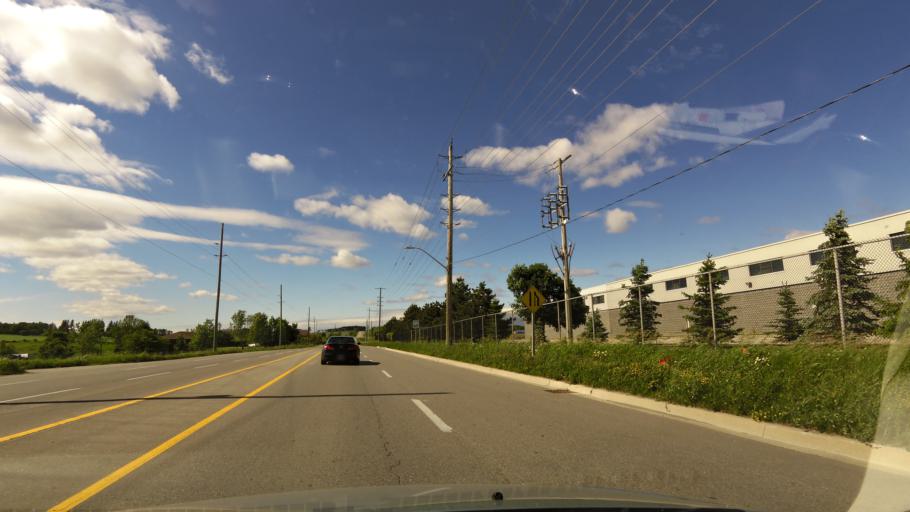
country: CA
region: Ontario
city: Bradford West Gwillimbury
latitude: 44.1118
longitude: -79.6032
